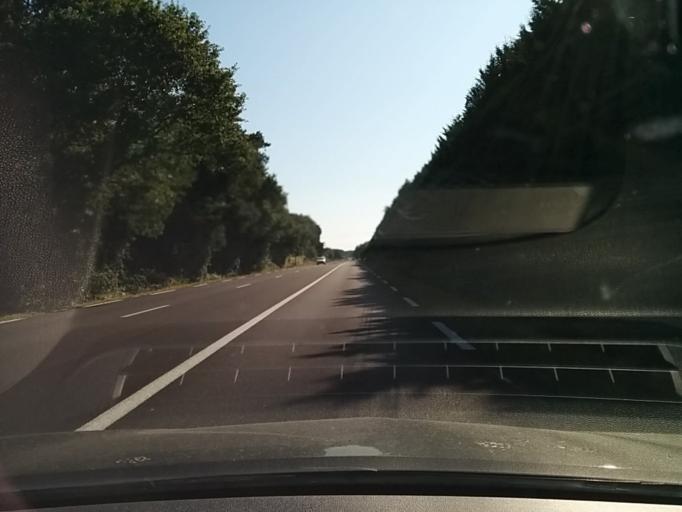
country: FR
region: Aquitaine
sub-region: Departement des Landes
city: Benesse-Maremne
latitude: 43.6237
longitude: -1.3808
